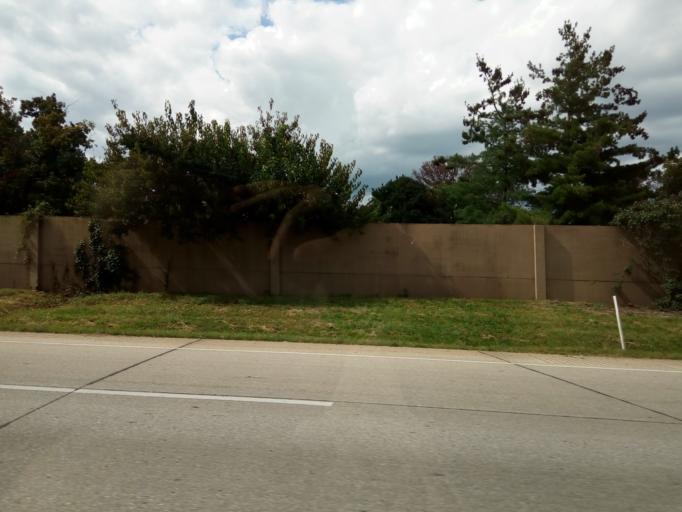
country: US
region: Kentucky
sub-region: Jefferson County
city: Saint Regis Park
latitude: 38.2257
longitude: -85.6420
